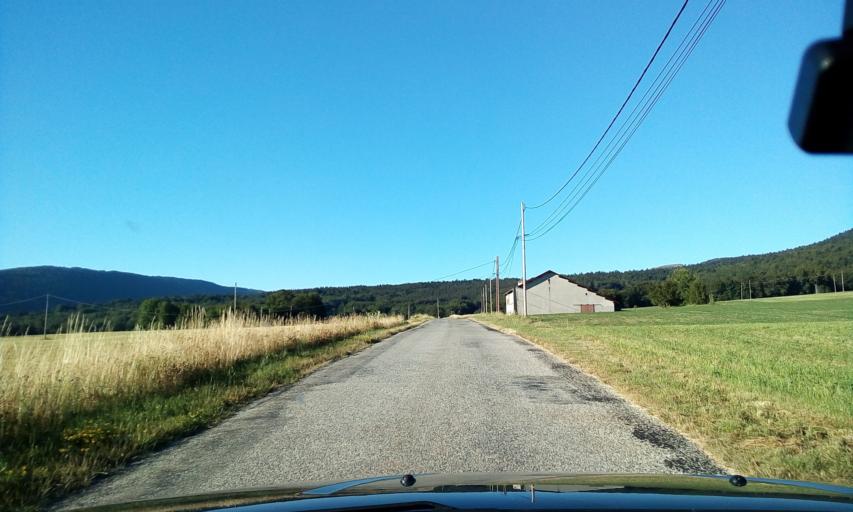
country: FR
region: Rhone-Alpes
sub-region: Departement de la Drome
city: Die
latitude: 44.8731
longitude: 5.3615
